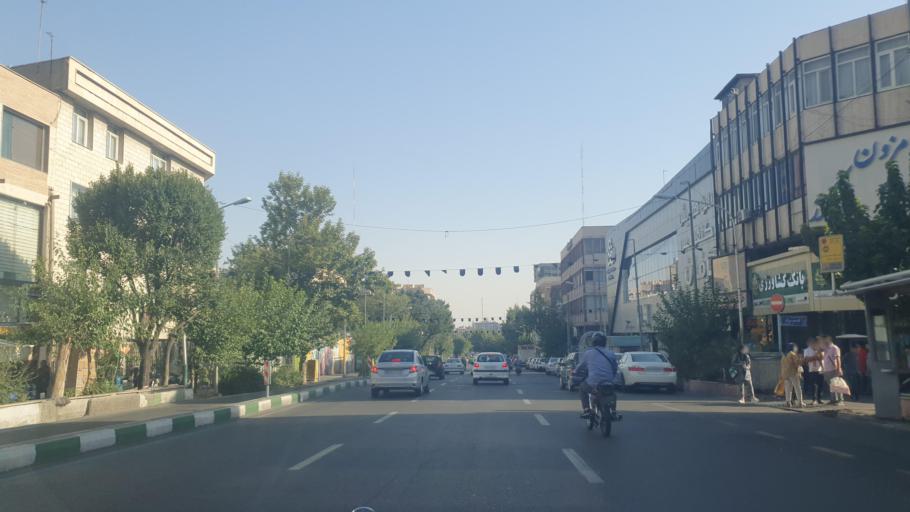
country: IR
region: Tehran
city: Tehran
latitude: 35.7142
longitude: 51.4258
